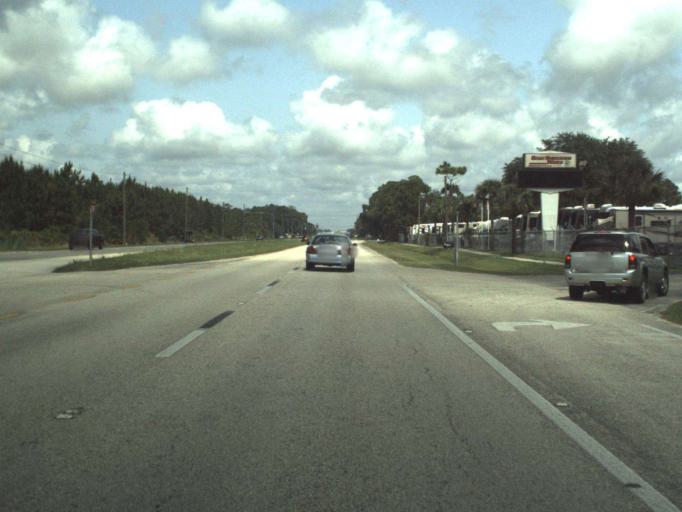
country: US
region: Florida
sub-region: Volusia County
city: Ormond-by-the-Sea
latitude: 29.3265
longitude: -81.1182
